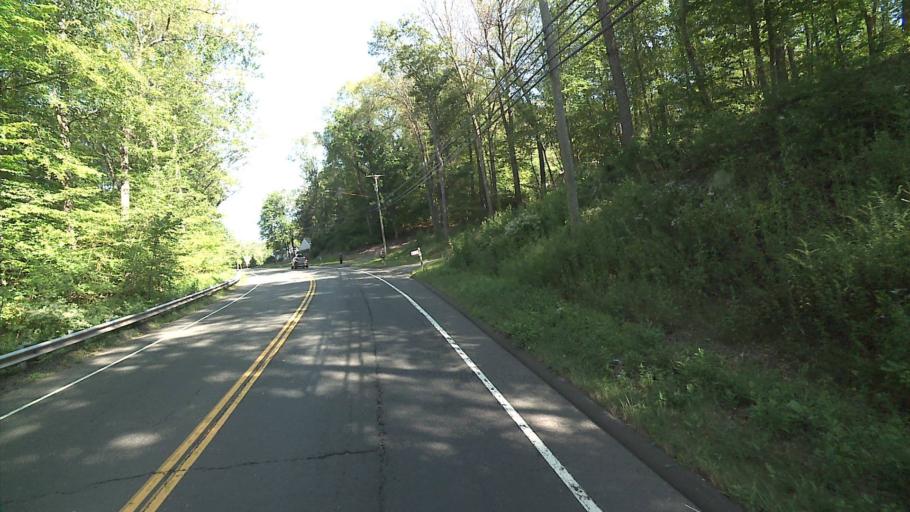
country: US
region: Connecticut
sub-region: New Haven County
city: Cheshire Village
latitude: 41.5353
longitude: -72.9386
